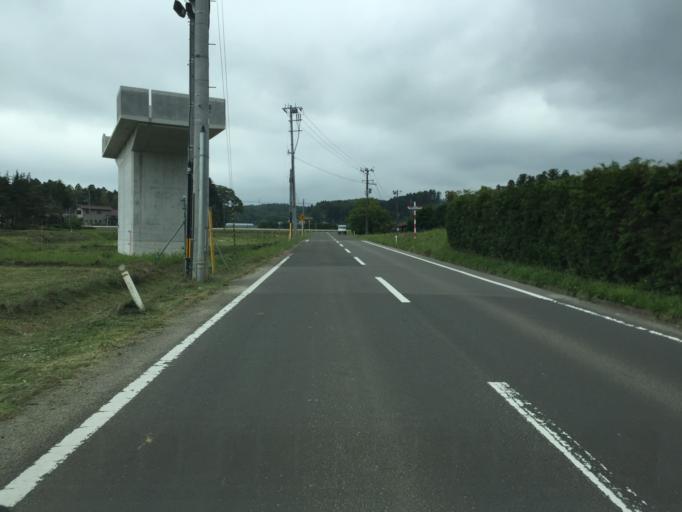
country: JP
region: Miyagi
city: Marumori
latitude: 37.7746
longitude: 140.8955
